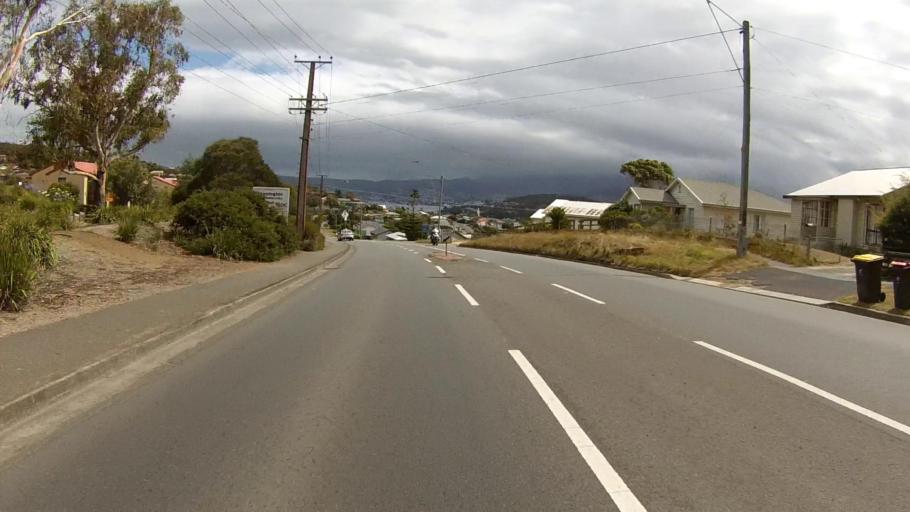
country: AU
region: Tasmania
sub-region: Clarence
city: Warrane
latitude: -42.8607
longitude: 147.3804
